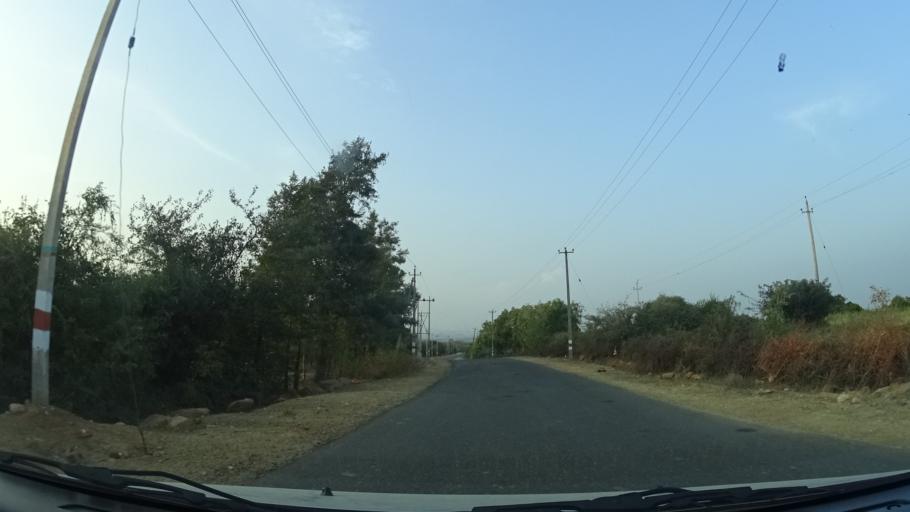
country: IN
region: Karnataka
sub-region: Bellary
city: Hampi
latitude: 15.2662
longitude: 76.4854
